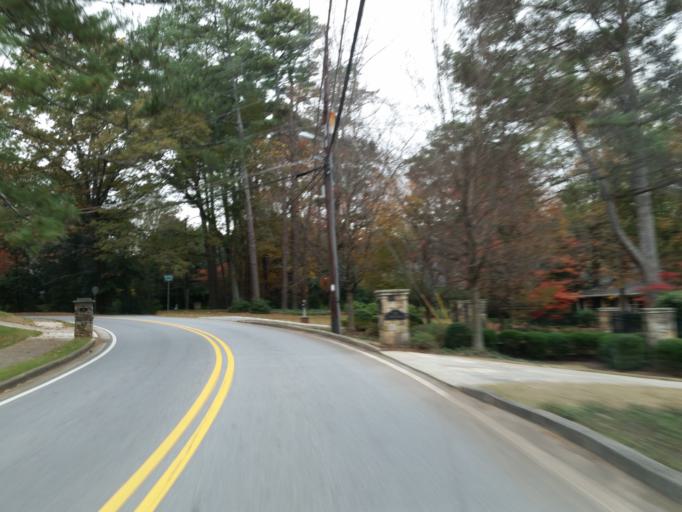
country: US
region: Georgia
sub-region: Fulton County
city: Sandy Springs
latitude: 33.8945
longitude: -84.3909
